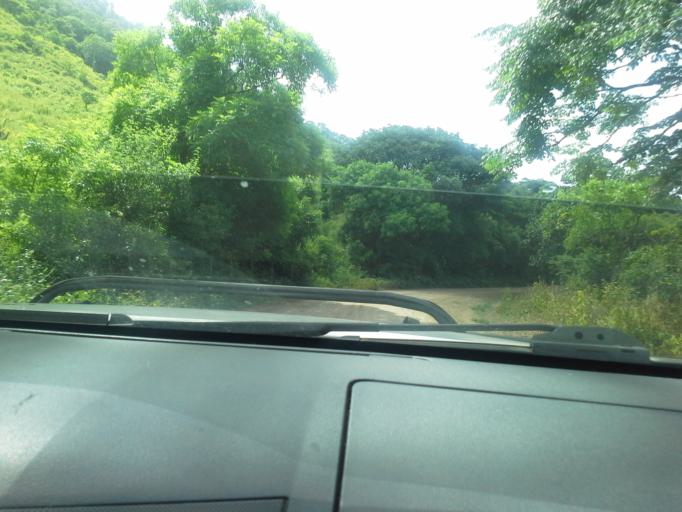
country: NI
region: Matagalpa
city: Terrabona
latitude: 12.7169
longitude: -85.9635
